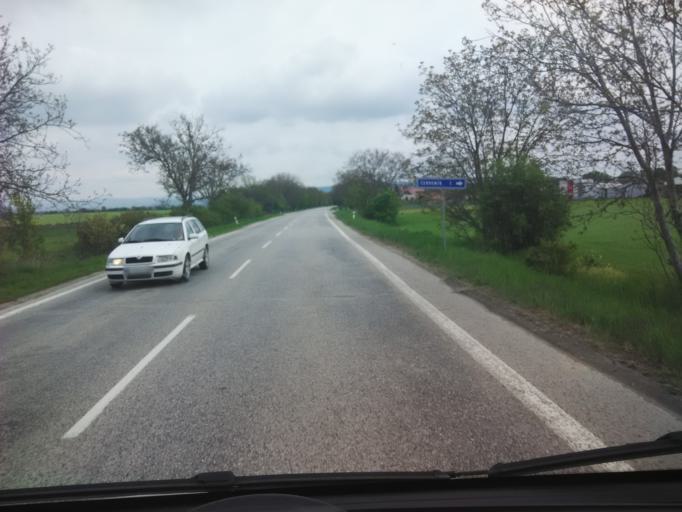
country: SK
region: Trnavsky
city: Leopoldov
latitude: 48.4624
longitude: 17.7484
